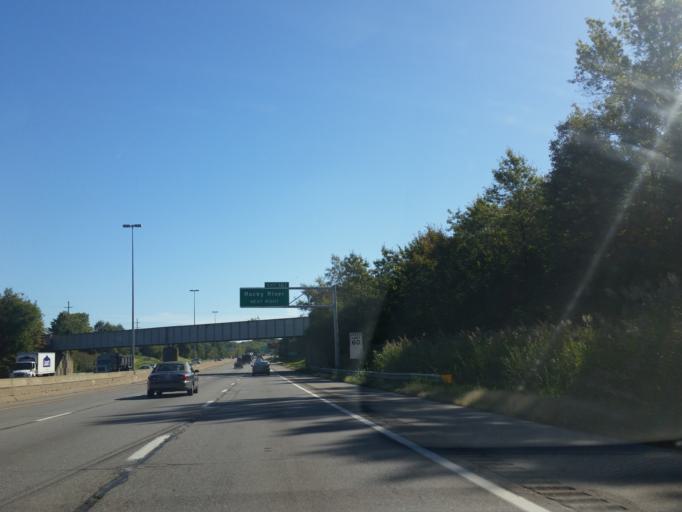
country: US
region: Ohio
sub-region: Cuyahoga County
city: Fairview Park
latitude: 41.4760
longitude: -81.8768
